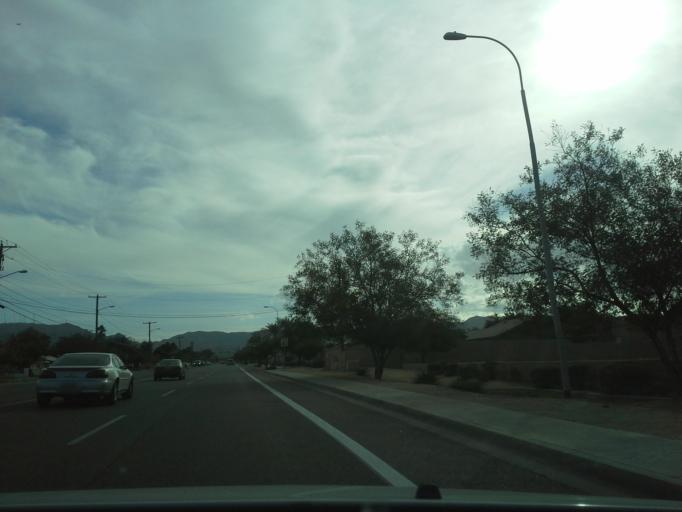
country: US
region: Arizona
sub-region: Maricopa County
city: Phoenix
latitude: 33.3882
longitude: -112.0820
